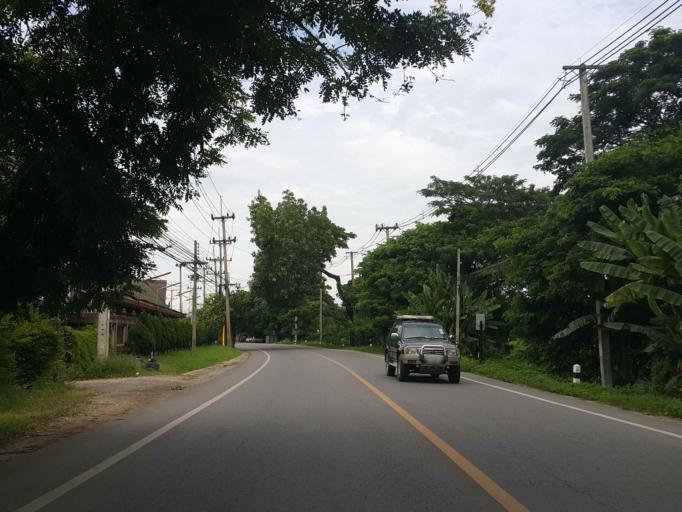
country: TH
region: Lamphun
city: Lamphun
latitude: 18.6221
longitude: 99.0342
